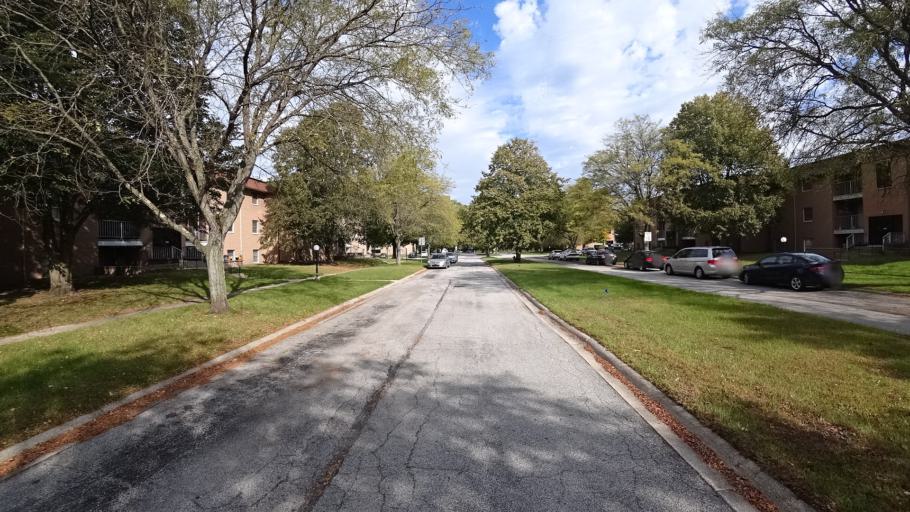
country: US
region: Indiana
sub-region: LaPorte County
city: Trail Creek
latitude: 41.6932
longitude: -86.8660
